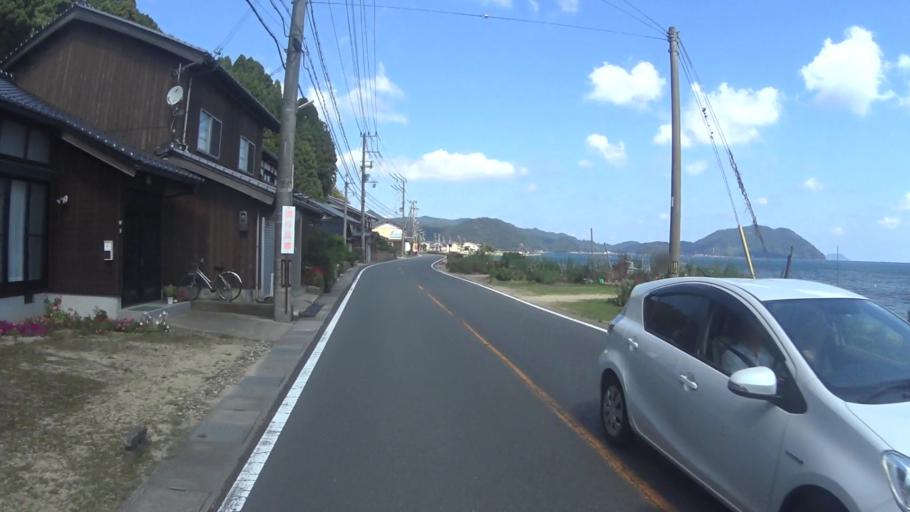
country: JP
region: Kyoto
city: Miyazu
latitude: 35.6519
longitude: 135.2550
